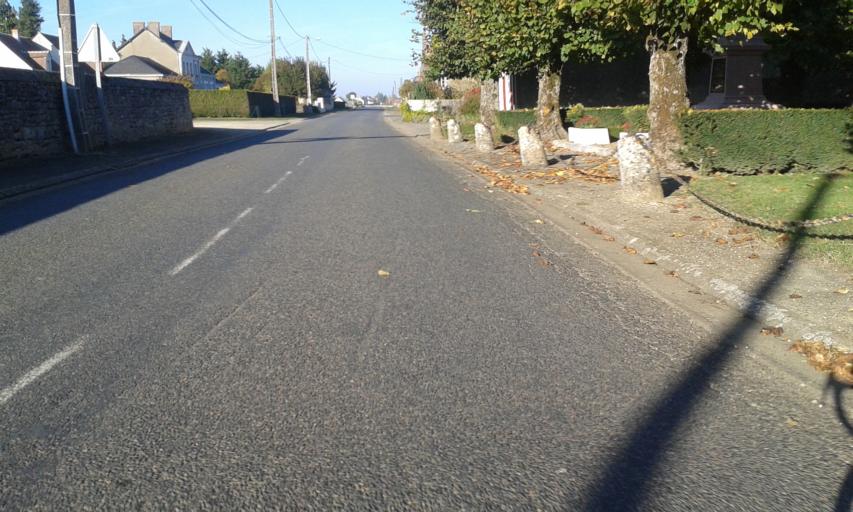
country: FR
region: Centre
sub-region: Departement du Loir-et-Cher
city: Oucques
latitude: 47.8889
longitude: 1.3711
